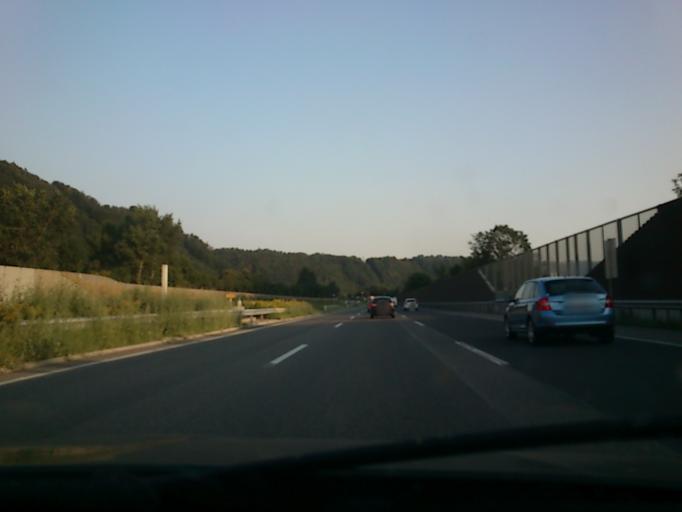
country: AT
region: Styria
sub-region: Politischer Bezirk Graz-Umgebung
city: Gratkorn
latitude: 47.1522
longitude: 15.3268
